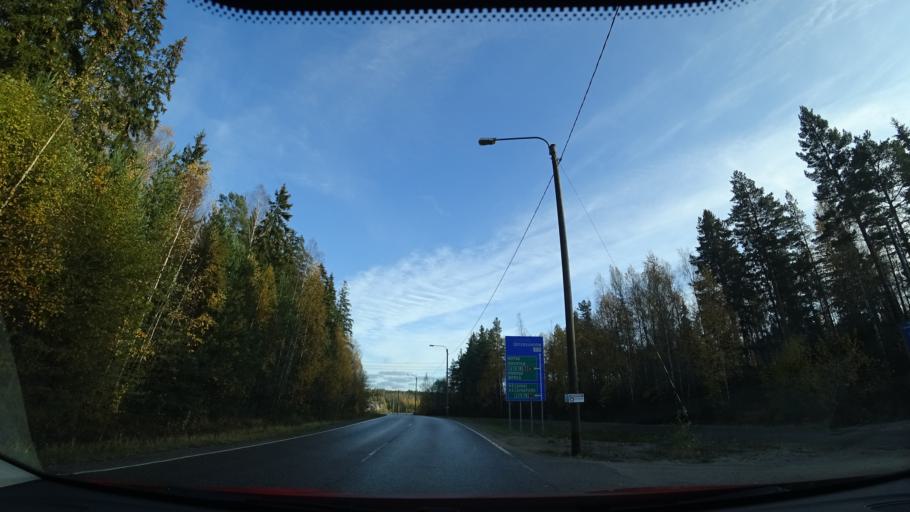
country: FI
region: Uusimaa
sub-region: Helsinki
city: Sibbo
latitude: 60.2695
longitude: 25.2046
